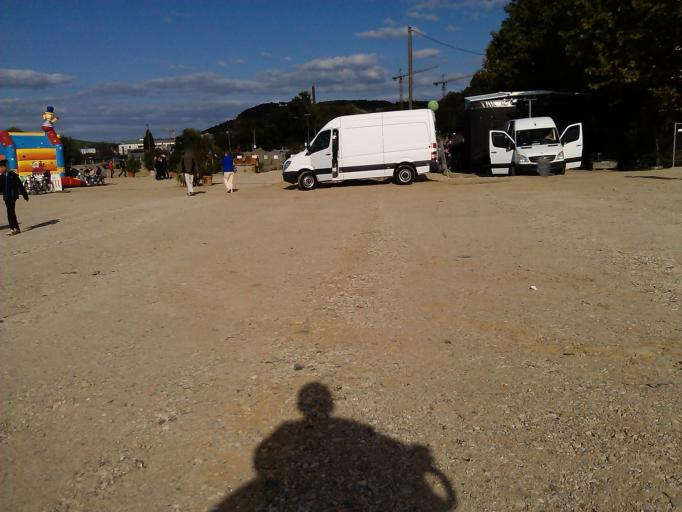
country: DE
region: Baden-Wuerttemberg
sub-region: Regierungsbezirk Stuttgart
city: Heilbronn
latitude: 49.1465
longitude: 9.2085
